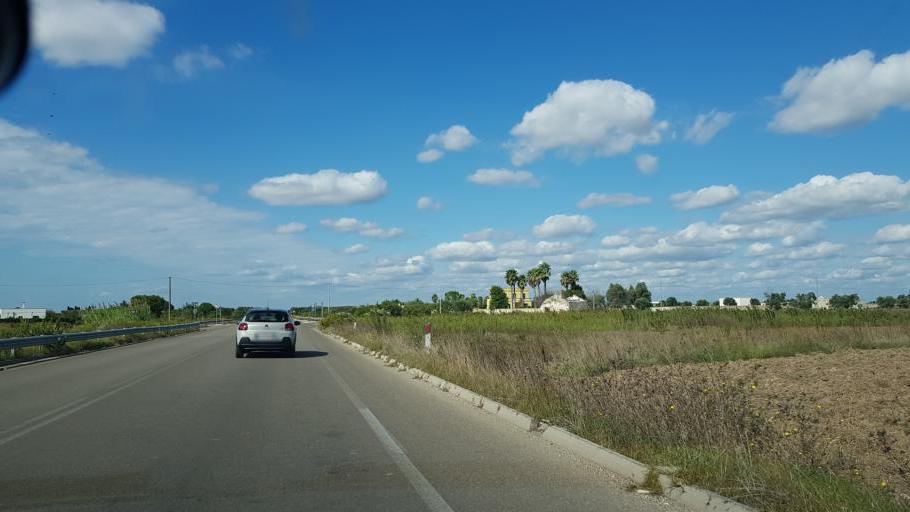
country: IT
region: Apulia
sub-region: Provincia di Lecce
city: Leverano
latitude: 40.3051
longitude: 18.0018
